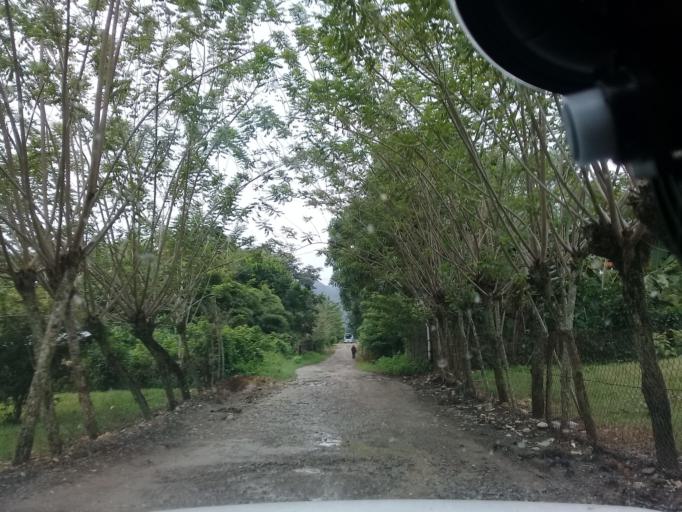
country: MX
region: Veracruz
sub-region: Chalma
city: San Pedro Coyutla
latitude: 21.2290
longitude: -98.4240
